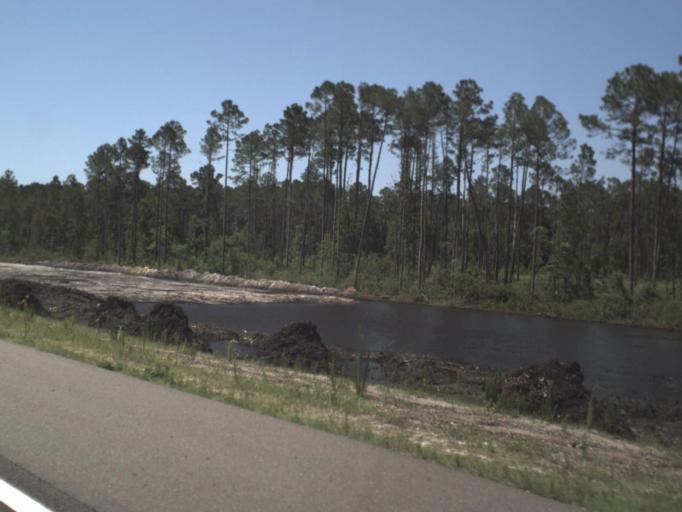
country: US
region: Florida
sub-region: Duval County
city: Baldwin
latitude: 30.2541
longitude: -81.8527
